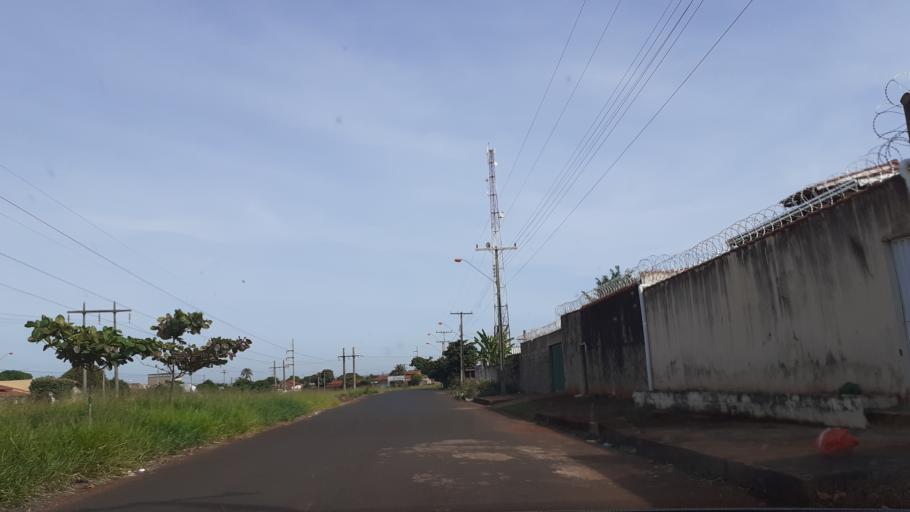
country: BR
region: Goias
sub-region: Itumbiara
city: Itumbiara
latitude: -18.4194
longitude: -49.2435
